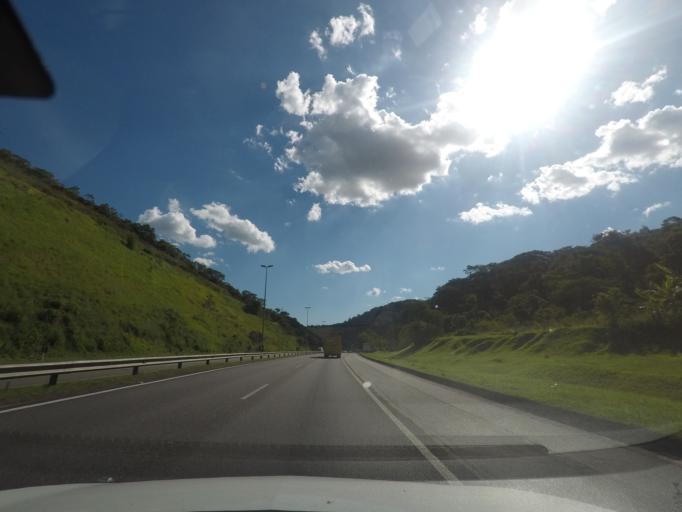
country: BR
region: Rio de Janeiro
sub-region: Guapimirim
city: Guapimirim
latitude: -22.5675
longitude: -43.0021
